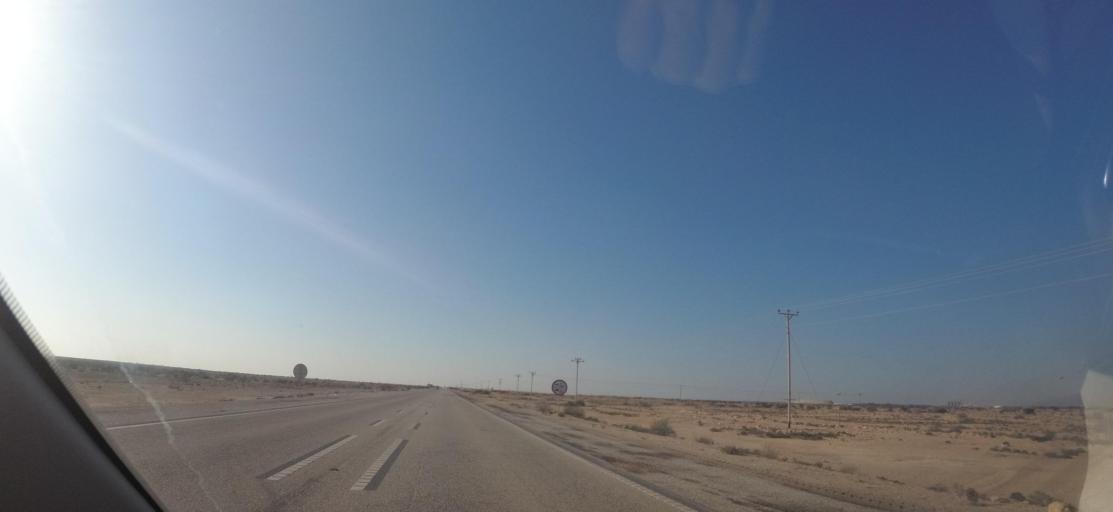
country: QA
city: Al Ghuwayriyah
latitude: 25.8571
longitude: 51.2520
